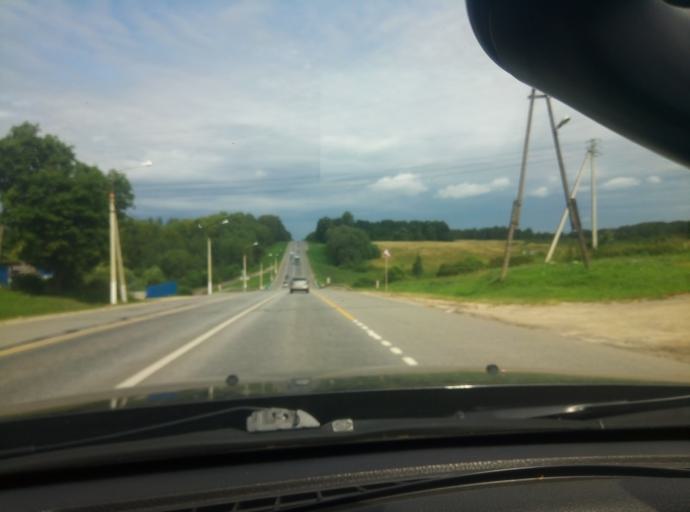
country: RU
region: Tula
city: Barsuki
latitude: 54.3529
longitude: 37.5367
